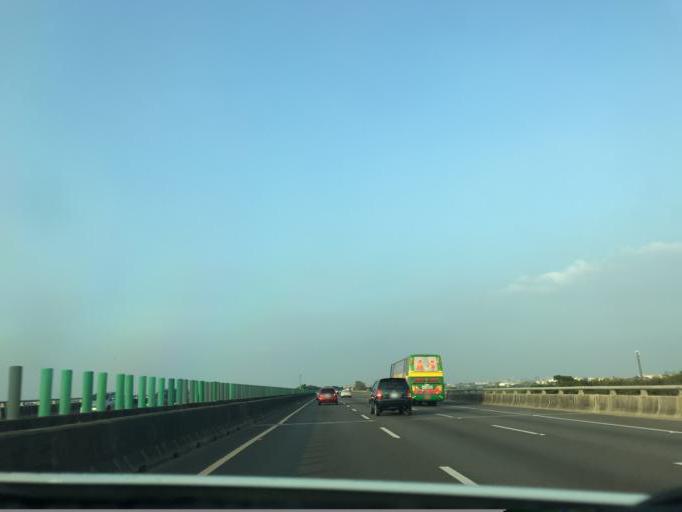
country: TW
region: Taiwan
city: Xinying
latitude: 23.2651
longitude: 120.2618
